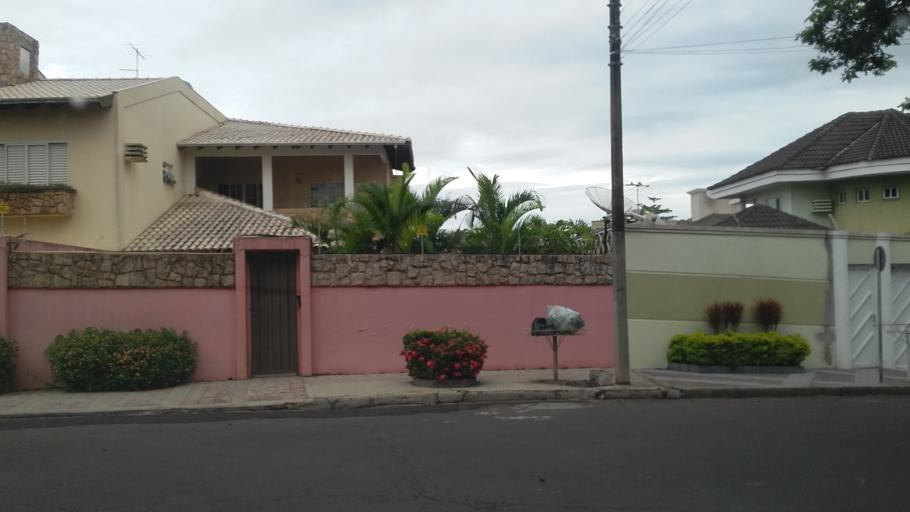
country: BR
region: Parana
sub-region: Londrina
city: Londrina
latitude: -23.3136
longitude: -51.1786
